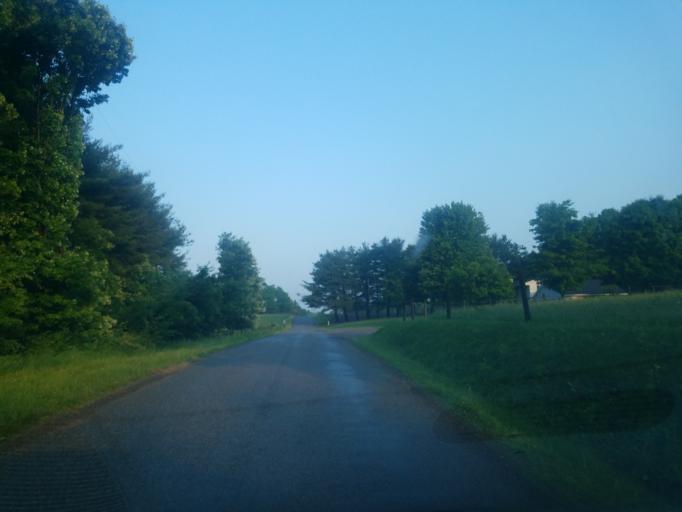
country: US
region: Ohio
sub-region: Stark County
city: Minerva
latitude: 40.7295
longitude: -81.0311
